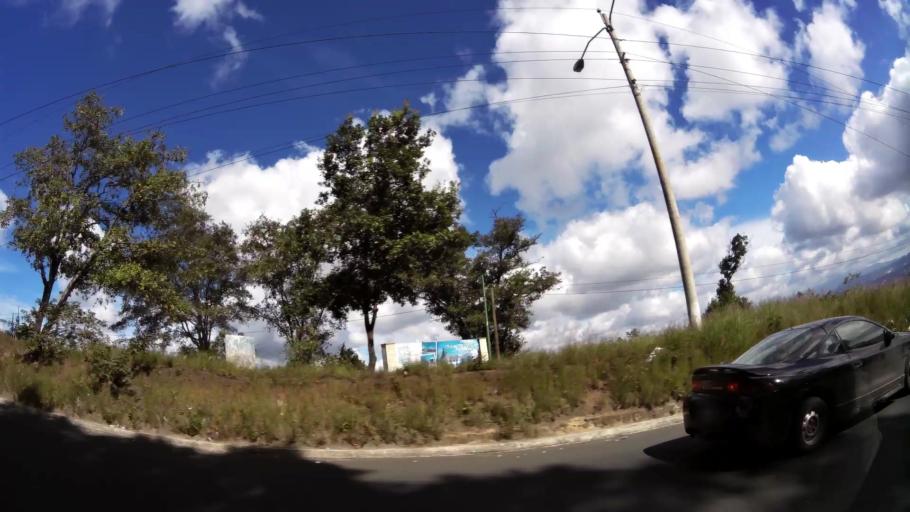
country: GT
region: Guatemala
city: Guatemala City
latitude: 14.6602
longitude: -90.5514
